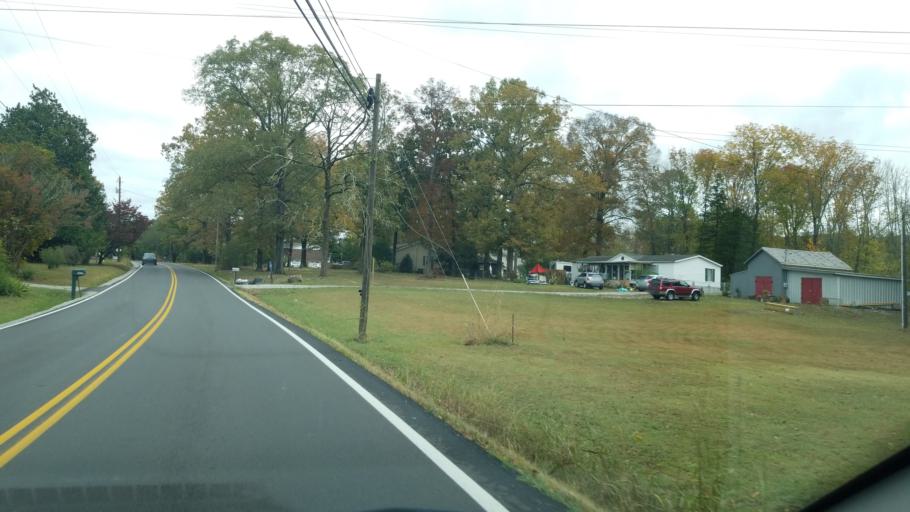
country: US
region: Tennessee
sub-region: Hamilton County
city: Collegedale
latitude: 35.0964
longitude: -85.0518
